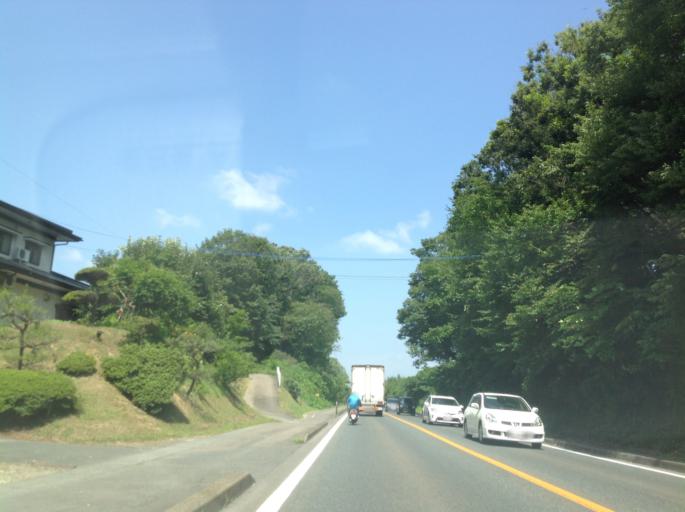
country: JP
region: Iwate
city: Hanamaki
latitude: 39.3486
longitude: 141.1086
